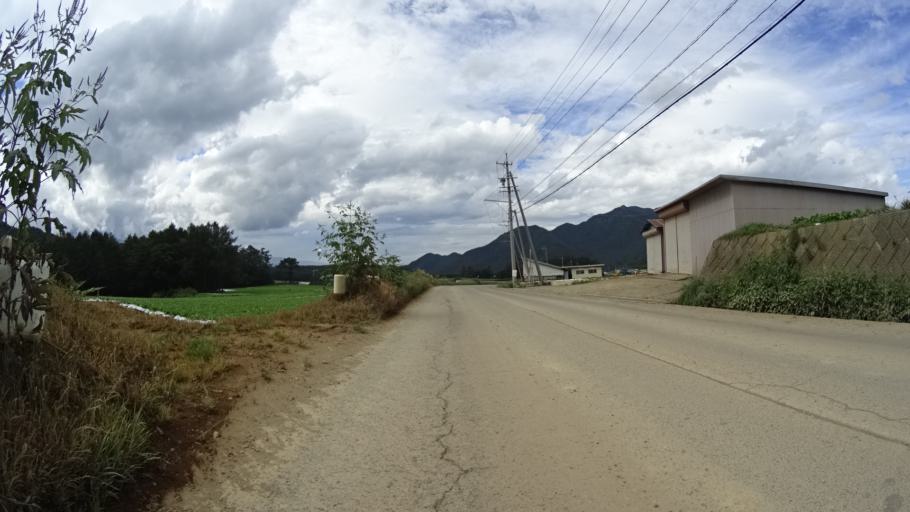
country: JP
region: Yamanashi
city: Nirasaki
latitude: 35.9519
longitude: 138.5475
